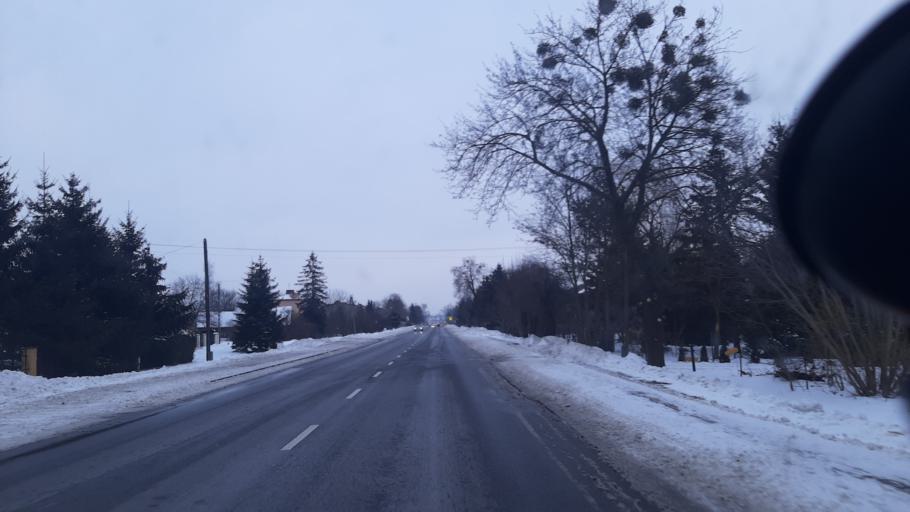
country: PL
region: Lublin Voivodeship
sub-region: Powiat pulawski
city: Markuszow
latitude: 51.3766
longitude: 22.2497
